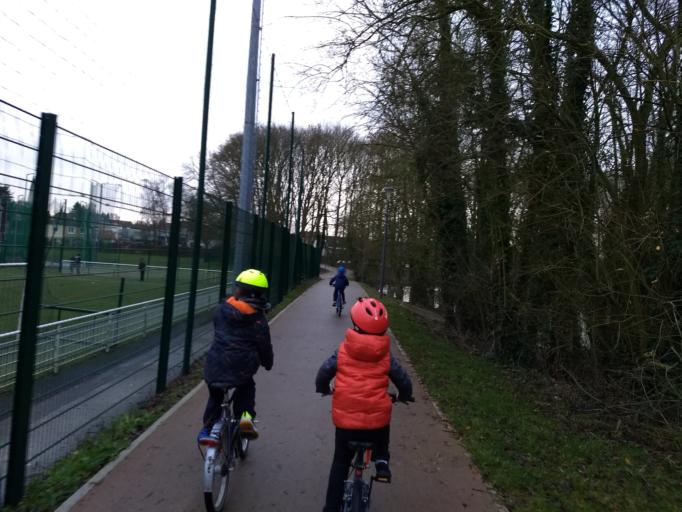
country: FR
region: Nord-Pas-de-Calais
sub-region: Departement du Pas-de-Calais
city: Achicourt
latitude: 50.2823
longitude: 2.7647
